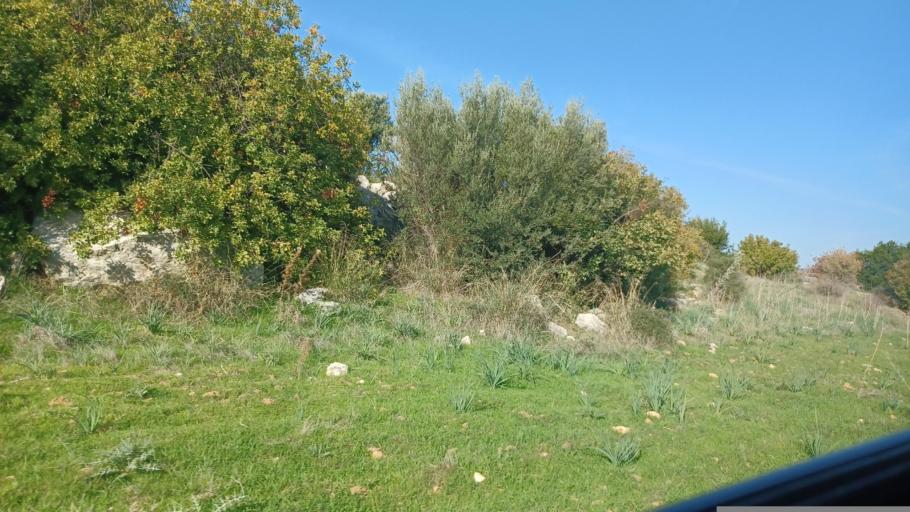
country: CY
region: Pafos
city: Mesogi
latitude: 34.7638
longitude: 32.5602
